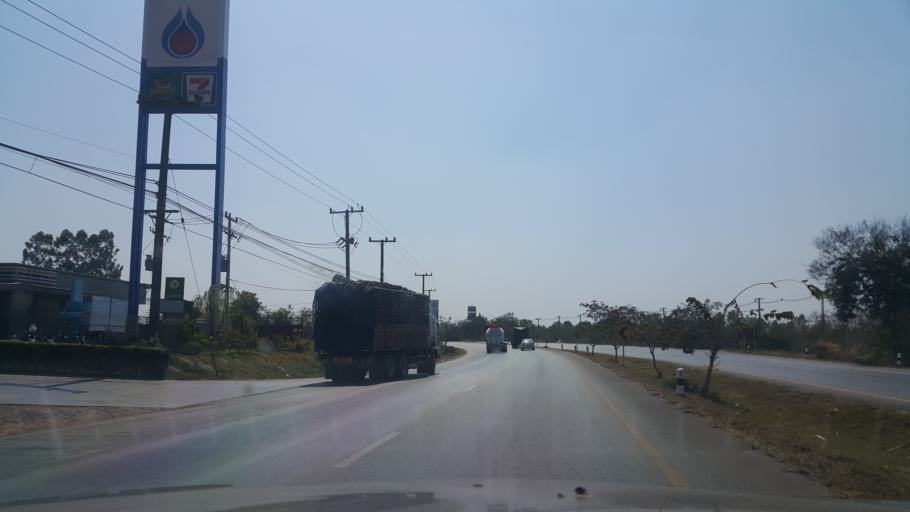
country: TH
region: Changwat Udon Thani
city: Non Sa-at
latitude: 17.0027
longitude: 102.8939
